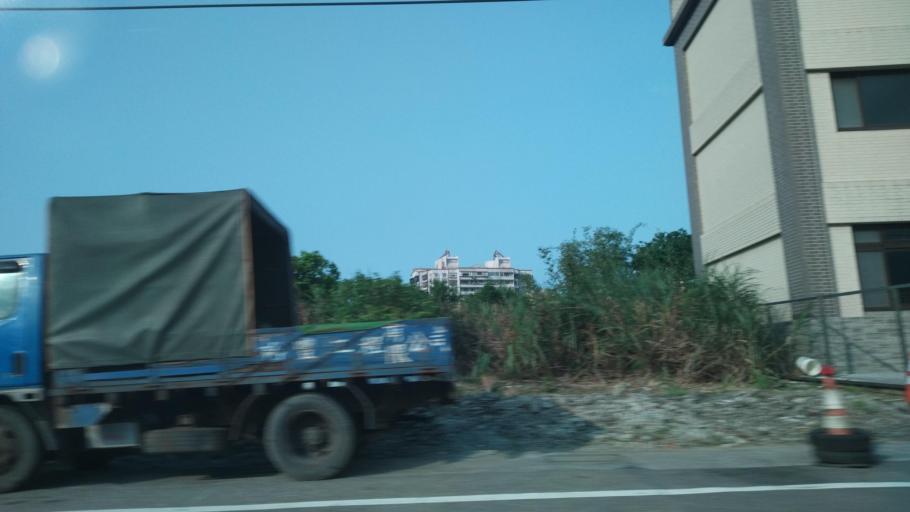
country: TW
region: Taiwan
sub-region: Keelung
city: Keelung
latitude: 25.2236
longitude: 121.6311
